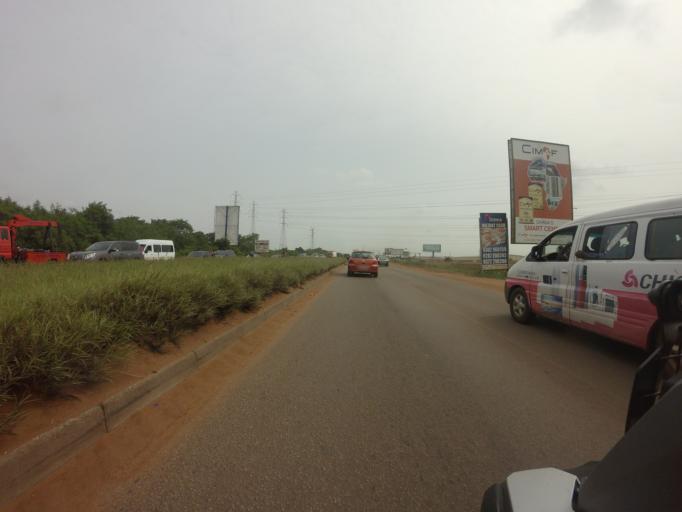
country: GH
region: Greater Accra
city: Tema
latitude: 5.6997
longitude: 0.0007
